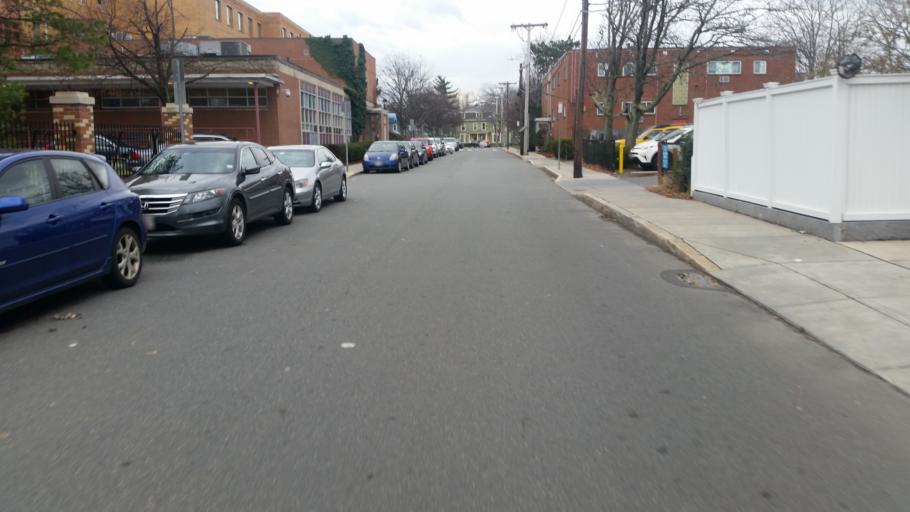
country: US
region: Massachusetts
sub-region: Middlesex County
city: Cambridge
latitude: 42.3764
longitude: -71.1075
